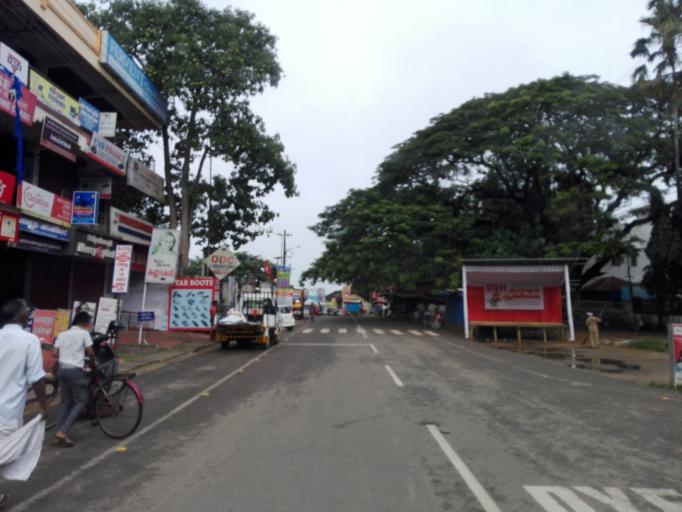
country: IN
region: Kerala
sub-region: Kottayam
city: Vaikam
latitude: 9.7496
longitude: 76.3904
